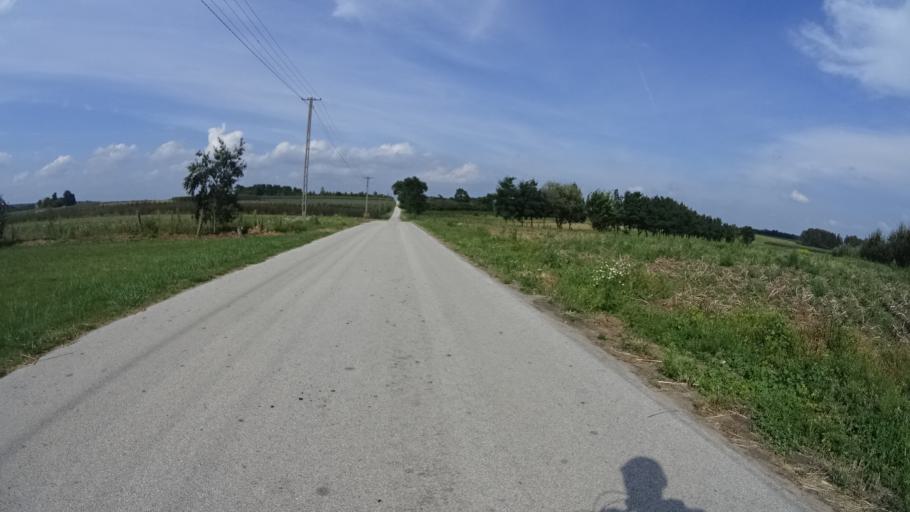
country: PL
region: Masovian Voivodeship
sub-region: Powiat grojecki
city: Goszczyn
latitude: 51.6864
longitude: 20.8431
